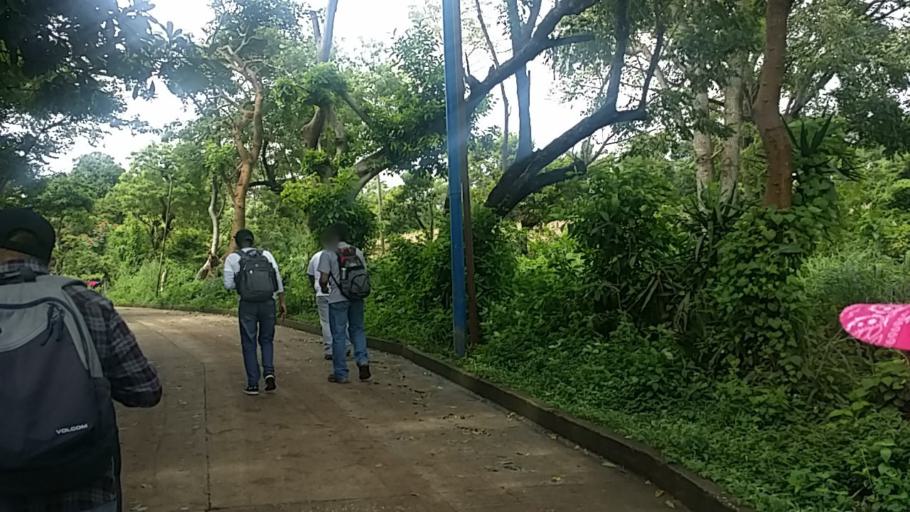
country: GT
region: Santa Rosa
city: Pueblo Nuevo Vinas
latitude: 14.3278
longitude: -90.5160
